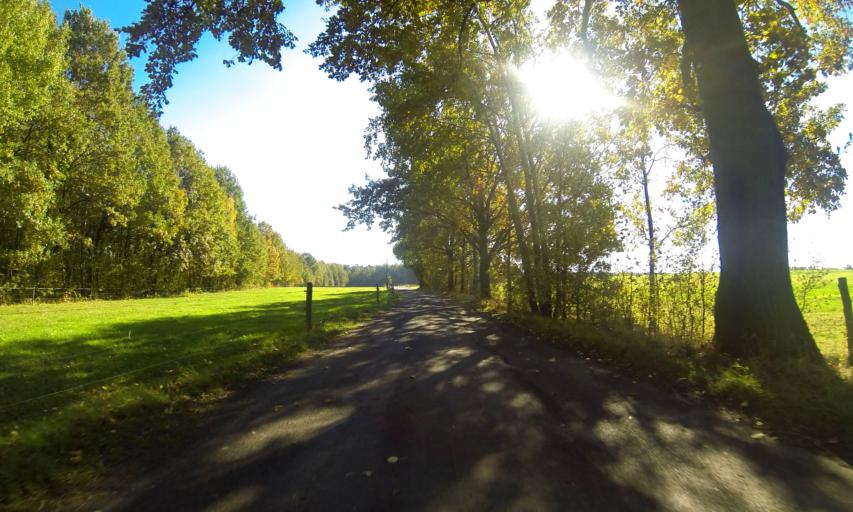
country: DE
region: Saxony
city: Weinbohla
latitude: 51.2057
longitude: 13.5938
